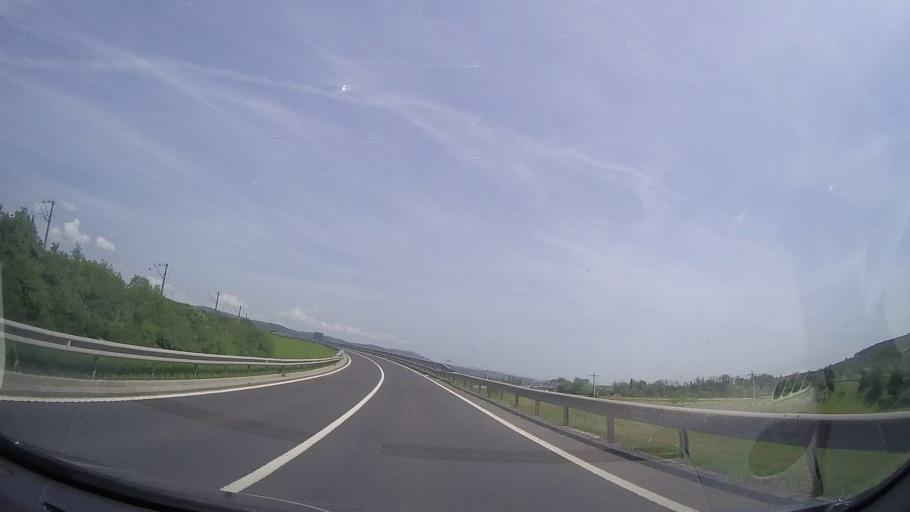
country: RO
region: Hunedoara
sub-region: Oras Simeria
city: Simeria
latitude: 45.8360
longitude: 23.0428
